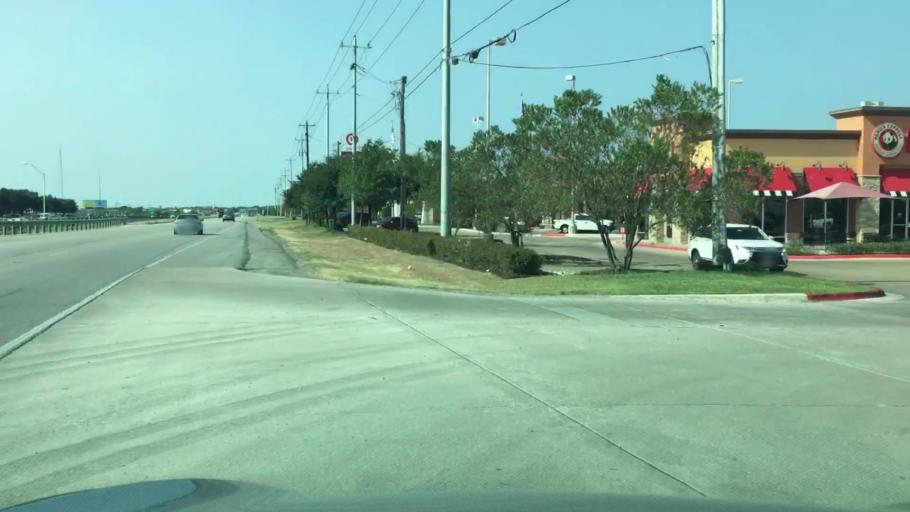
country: US
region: Texas
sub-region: Hays County
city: Kyle
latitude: 30.0124
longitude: -97.8617
